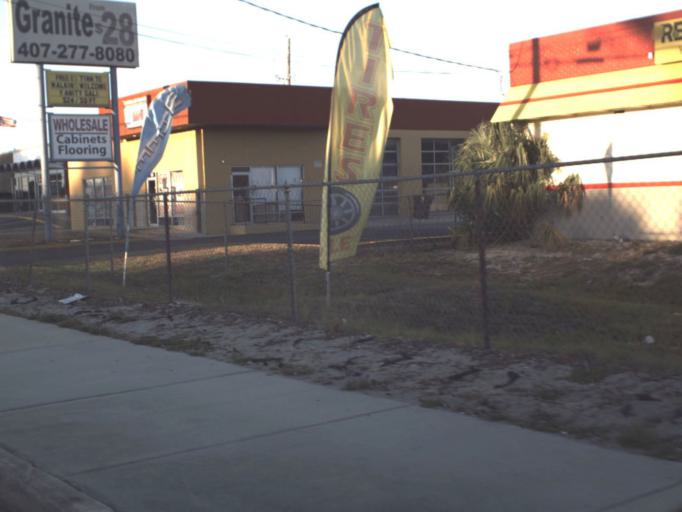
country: US
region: Florida
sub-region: Orange County
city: Azalea Park
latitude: 28.5476
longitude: -81.3106
